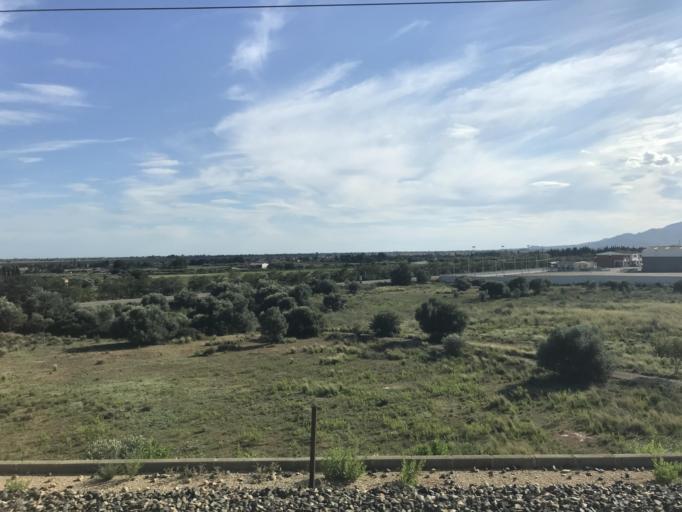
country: ES
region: Catalonia
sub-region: Provincia de Tarragona
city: Camarles
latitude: 40.7594
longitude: 0.6362
